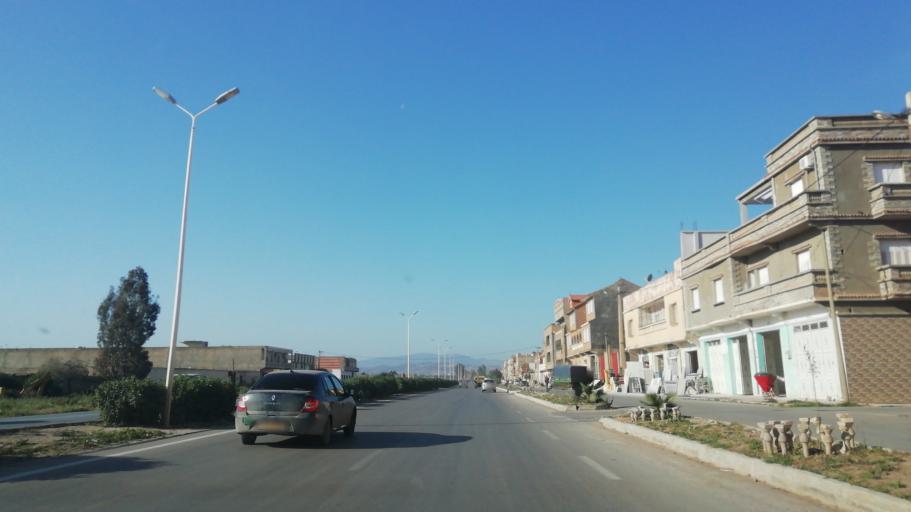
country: DZ
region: Mascara
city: Mascara
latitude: 35.6152
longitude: 0.1052
